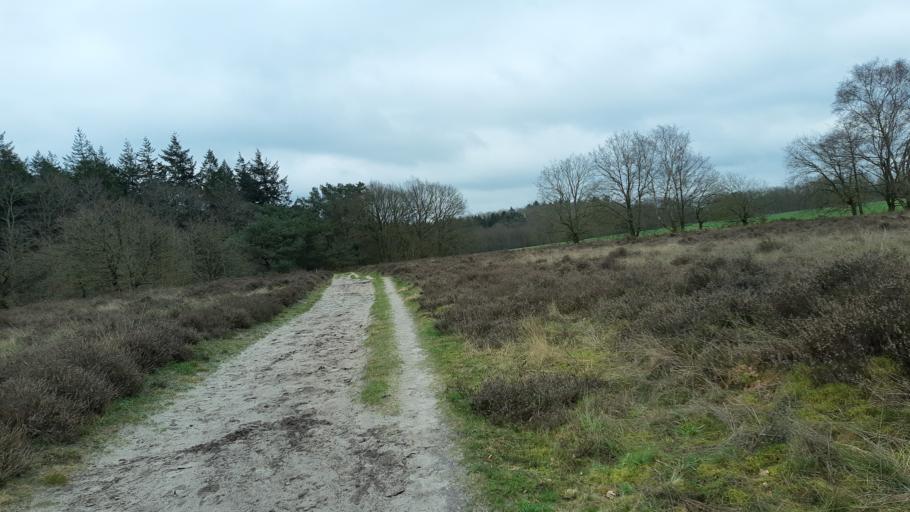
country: NL
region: Drenthe
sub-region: Gemeente Assen
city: Assen
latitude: 52.8488
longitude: 6.5863
